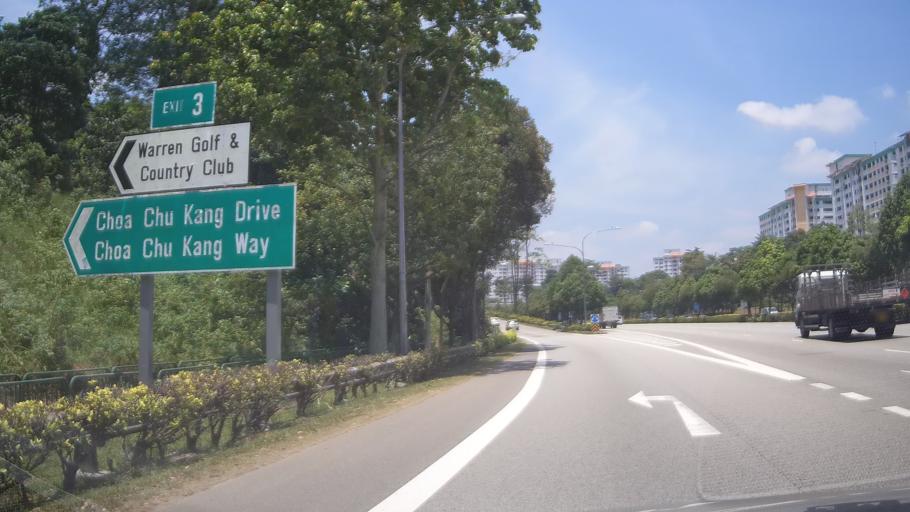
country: MY
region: Johor
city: Johor Bahru
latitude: 1.3895
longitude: 103.7489
